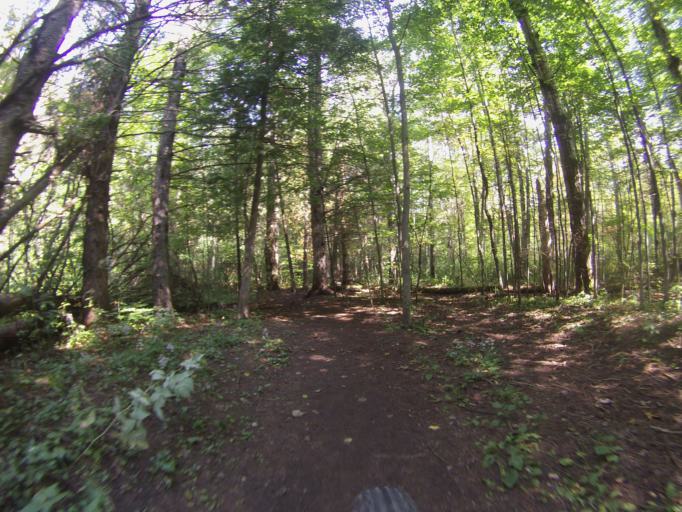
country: CA
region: Ontario
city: Ottawa
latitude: 45.3538
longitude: -75.6208
